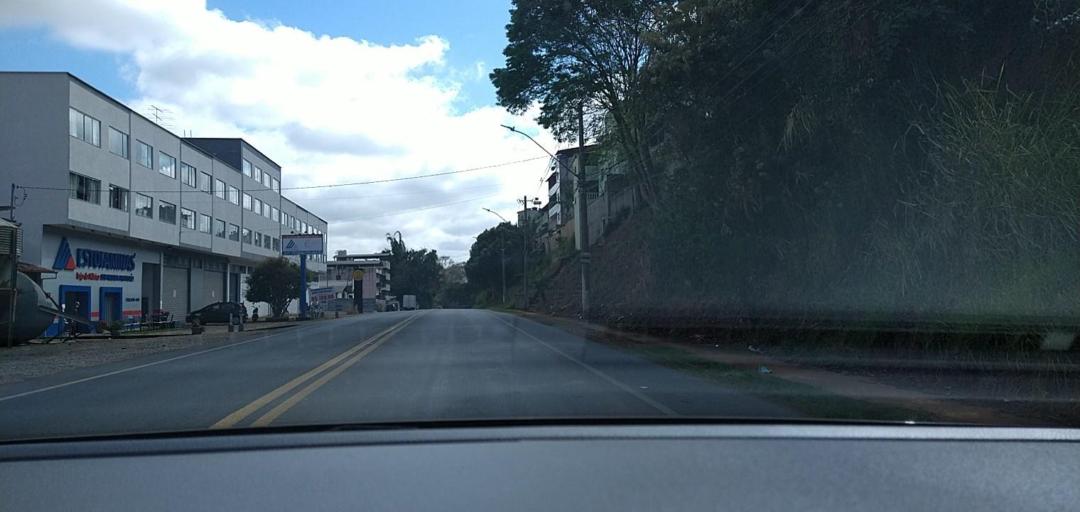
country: BR
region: Minas Gerais
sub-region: Vicosa
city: Vicosa
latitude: -20.7234
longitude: -42.8653
